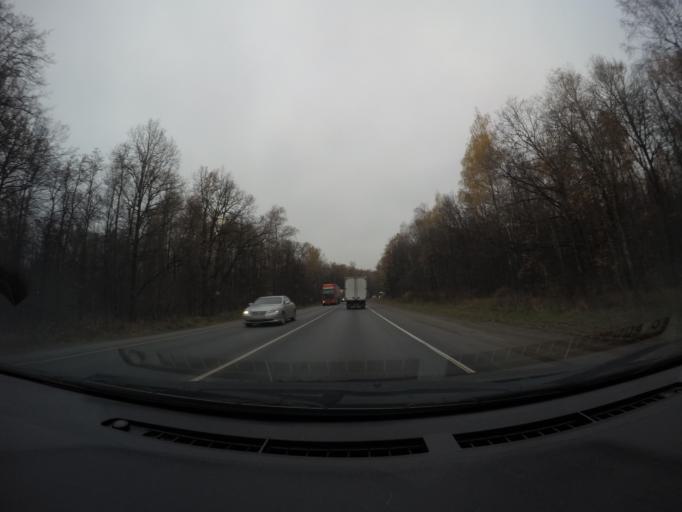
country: RU
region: Moskovskaya
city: Bronnitsy
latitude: 55.3976
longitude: 38.2236
